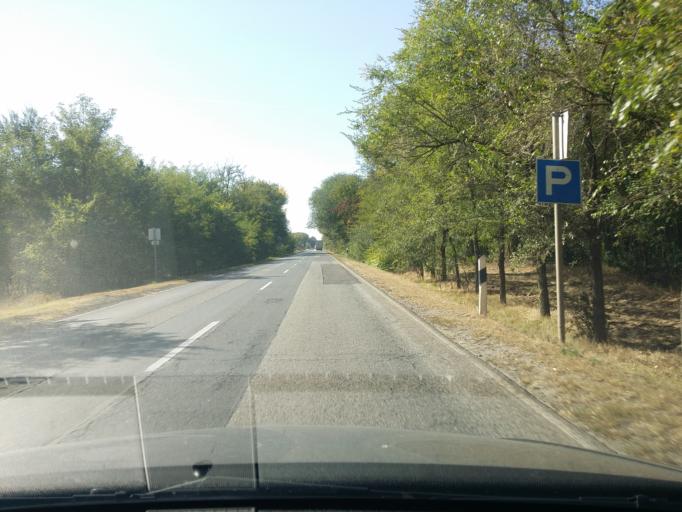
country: HU
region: Bacs-Kiskun
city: Lakitelek
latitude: 46.8790
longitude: 19.9850
